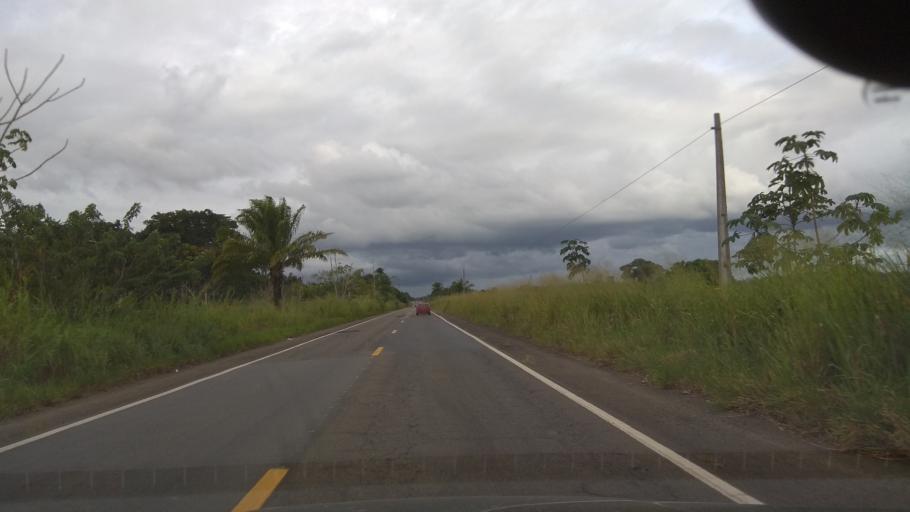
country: BR
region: Bahia
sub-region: Ubata
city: Ubata
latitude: -14.1954
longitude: -39.6336
